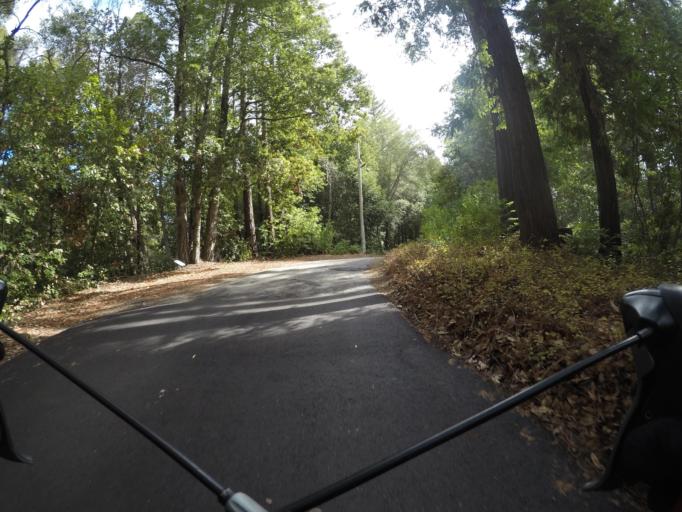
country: US
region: California
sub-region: Santa Cruz County
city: Brookdale
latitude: 37.1073
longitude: -122.0887
